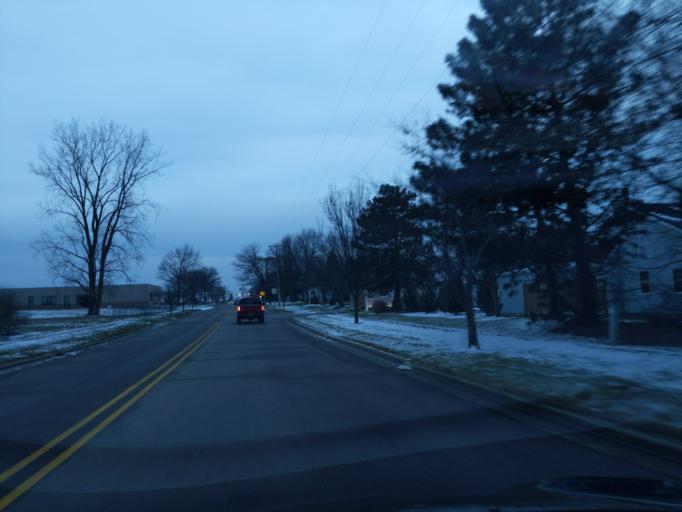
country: US
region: Michigan
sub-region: Ingham County
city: Mason
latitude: 42.5764
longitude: -84.4529
